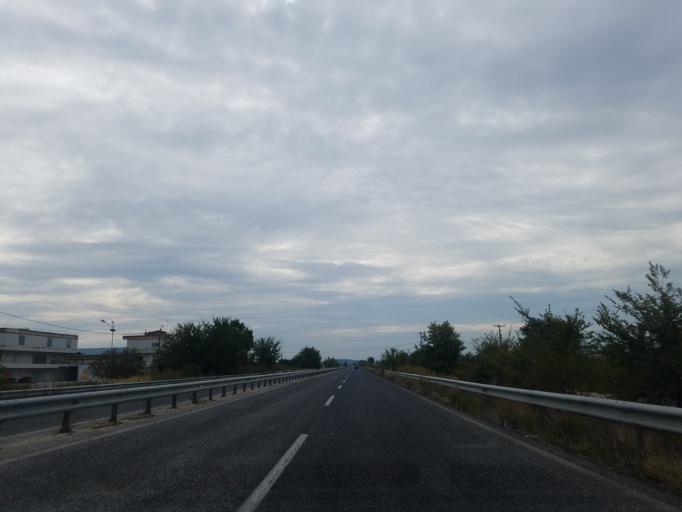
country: GR
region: Thessaly
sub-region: Trikala
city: Vasiliki
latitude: 39.6131
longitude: 21.7190
